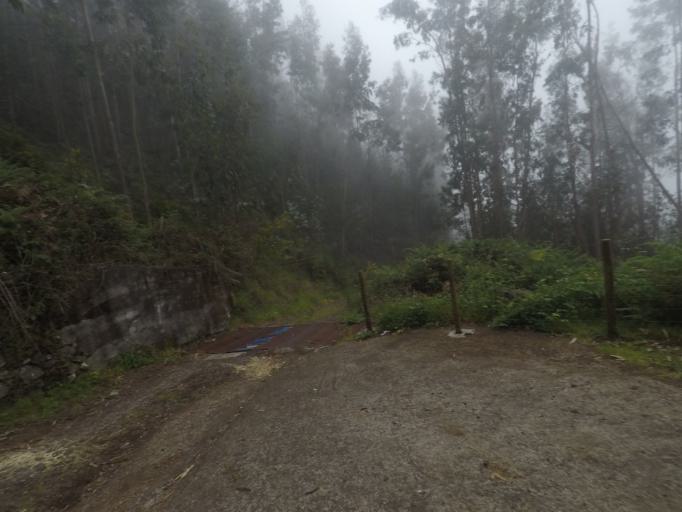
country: PT
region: Madeira
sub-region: Calheta
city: Arco da Calheta
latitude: 32.7295
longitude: -17.0958
